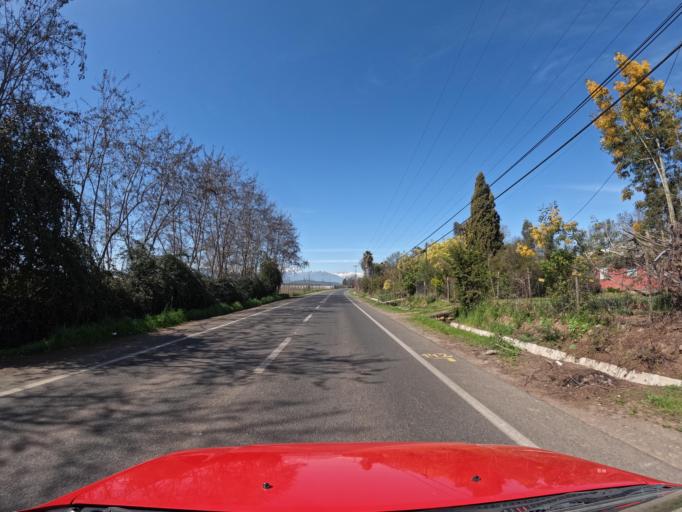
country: CL
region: Maule
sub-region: Provincia de Curico
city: Teno
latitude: -34.9655
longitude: -71.0406
